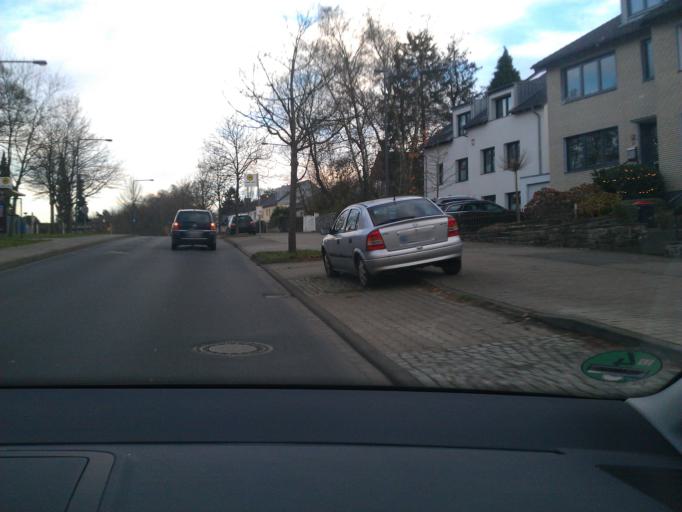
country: DE
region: North Rhine-Westphalia
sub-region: Regierungsbezirk Koln
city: Aachen
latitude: 50.7523
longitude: 6.1063
